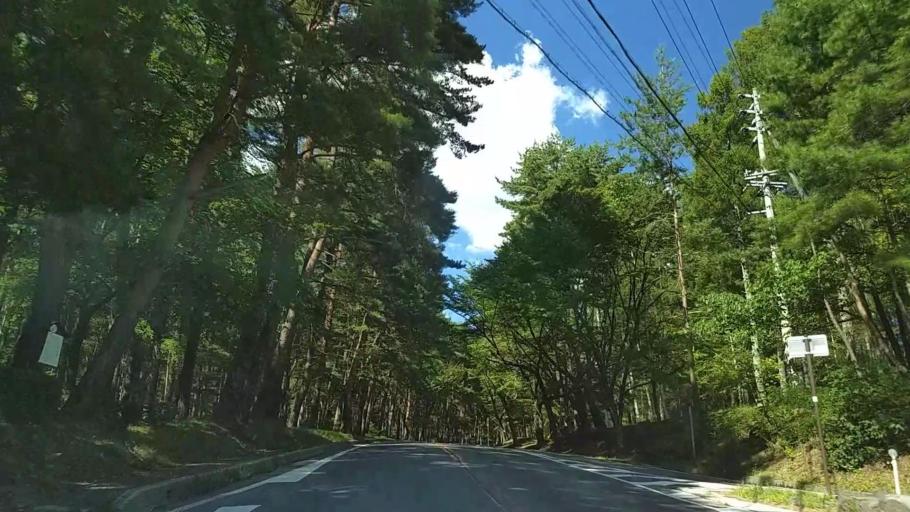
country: JP
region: Nagano
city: Chino
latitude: 36.0440
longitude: 138.2481
